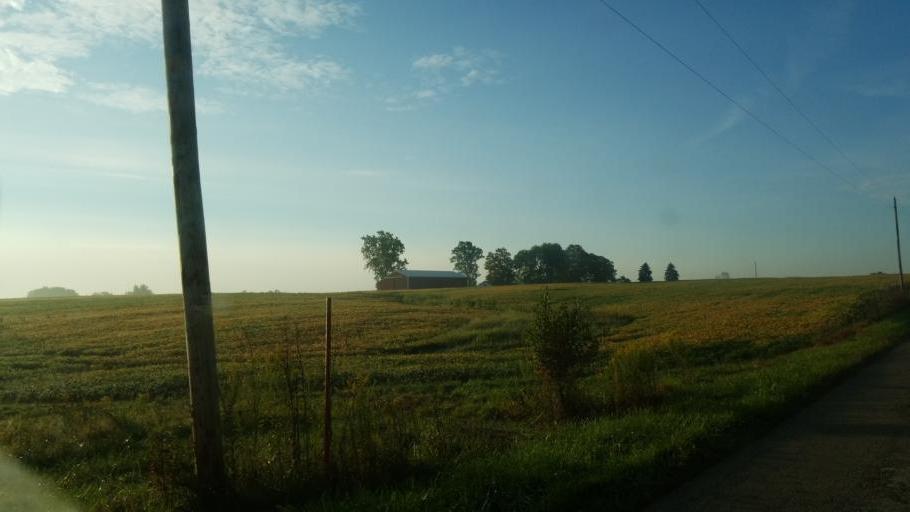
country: US
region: Ohio
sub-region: Knox County
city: Fredericktown
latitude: 40.4140
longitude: -82.5630
